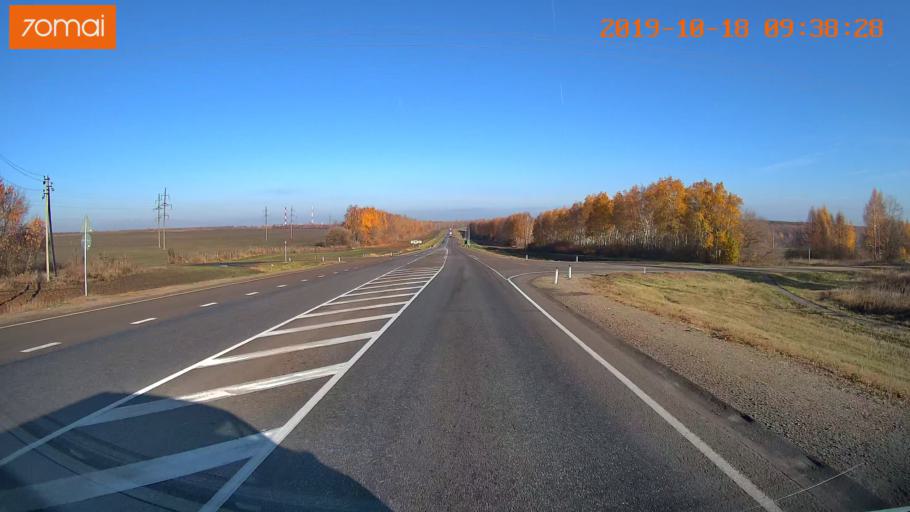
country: RU
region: Tula
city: Yefremov
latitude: 53.2383
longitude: 38.1370
